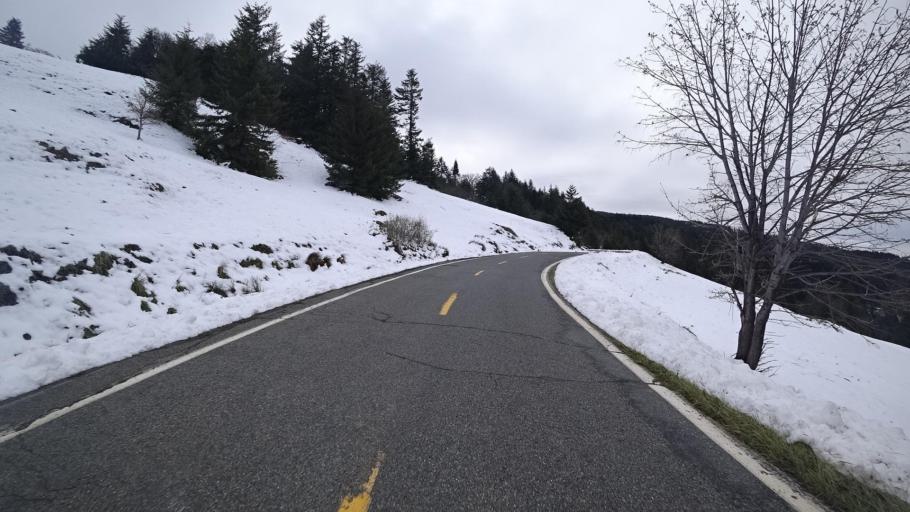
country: US
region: California
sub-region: Humboldt County
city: Willow Creek
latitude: 40.8701
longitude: -123.7509
